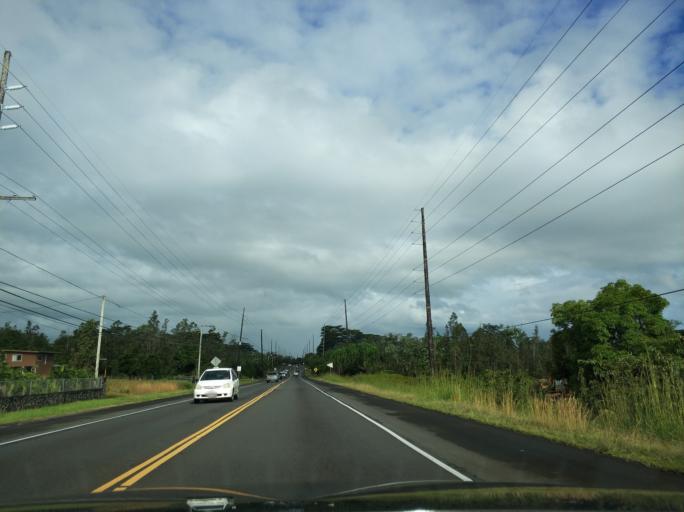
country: US
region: Hawaii
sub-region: Hawaii County
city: Orchidlands Estates
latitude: 19.5669
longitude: -154.9972
